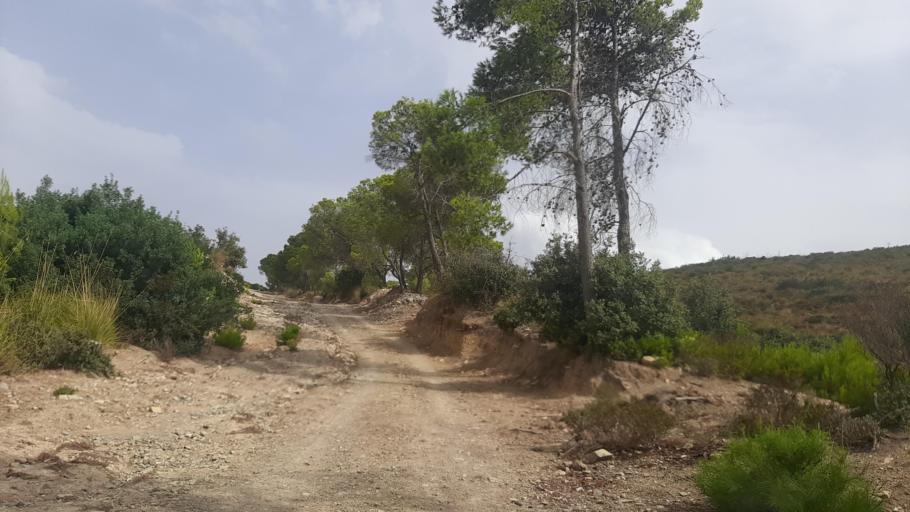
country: TN
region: Zaghwan
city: El Fahs
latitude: 36.1963
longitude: 9.8500
